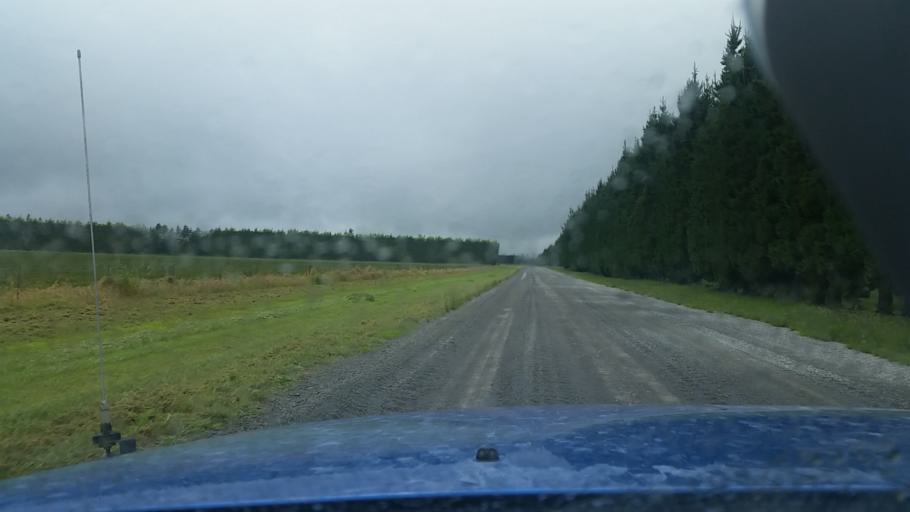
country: NZ
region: Canterbury
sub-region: Ashburton District
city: Methven
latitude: -43.6618
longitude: 171.7921
